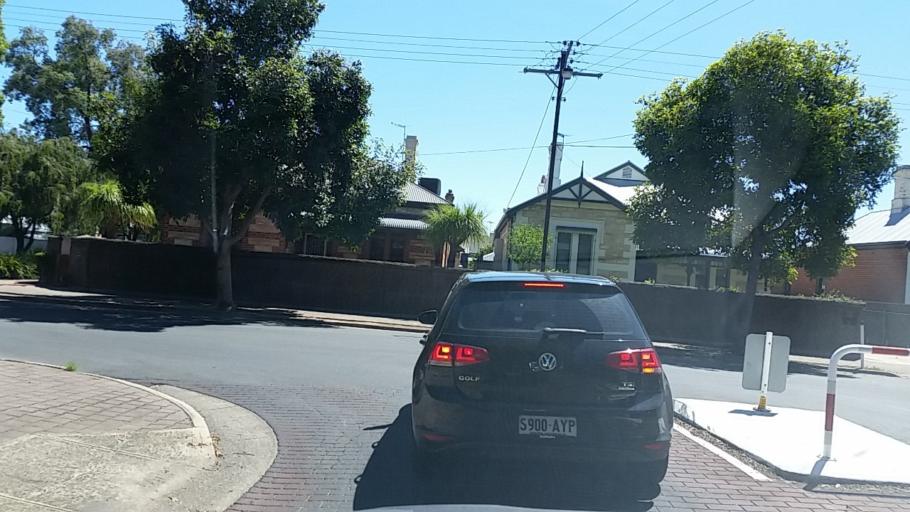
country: AU
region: South Australia
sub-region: Unley
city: Fullarton
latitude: -34.9481
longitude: 138.6215
